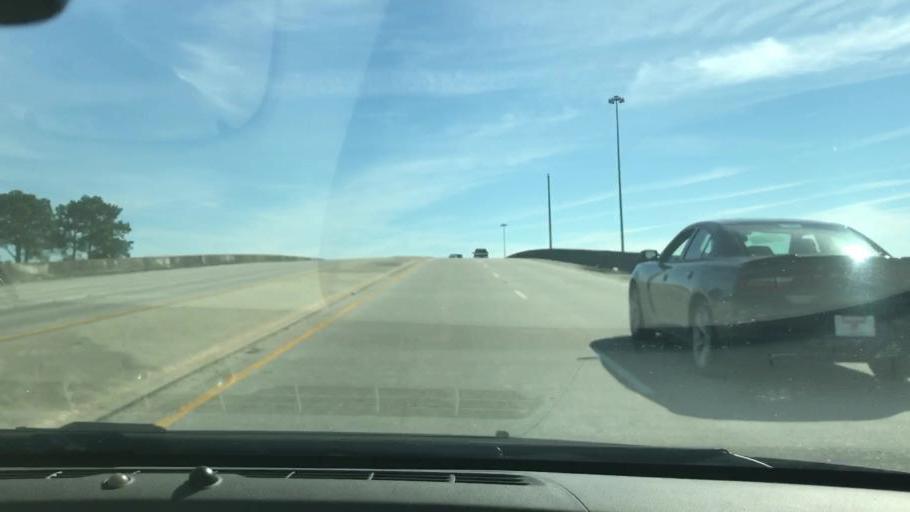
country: US
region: Louisiana
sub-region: Saint Tammany Parish
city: Eden Isle
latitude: 30.2226
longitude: -89.7839
